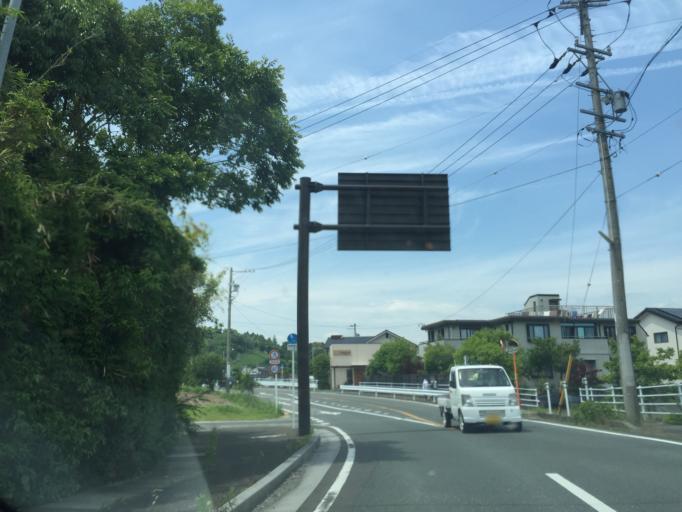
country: JP
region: Shizuoka
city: Kakegawa
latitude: 34.7920
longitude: 138.0083
